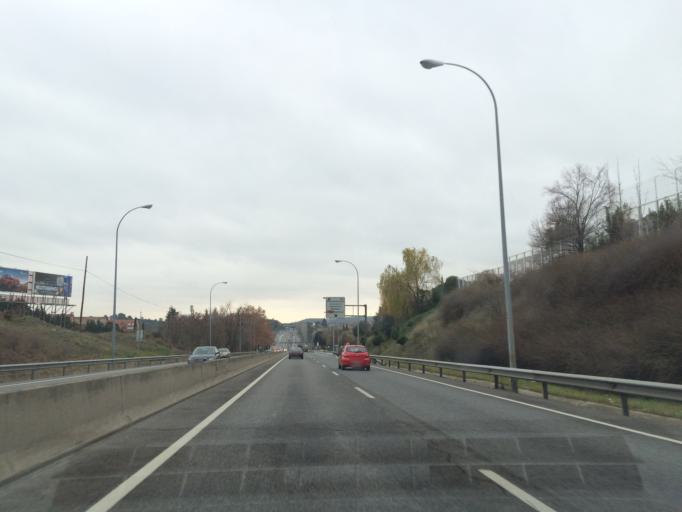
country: ES
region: Madrid
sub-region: Provincia de Madrid
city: Moncloa-Aravaca
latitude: 40.4585
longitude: -3.7695
